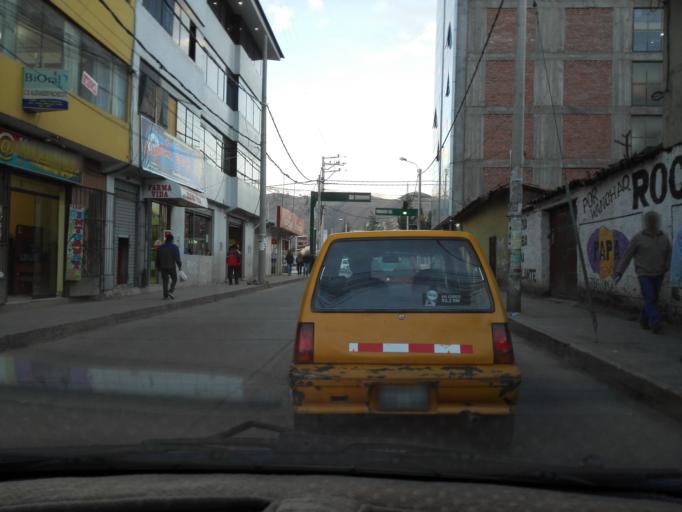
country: PE
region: Cusco
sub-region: Provincia de Cusco
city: Cusco
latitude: -13.5235
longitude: -71.9610
